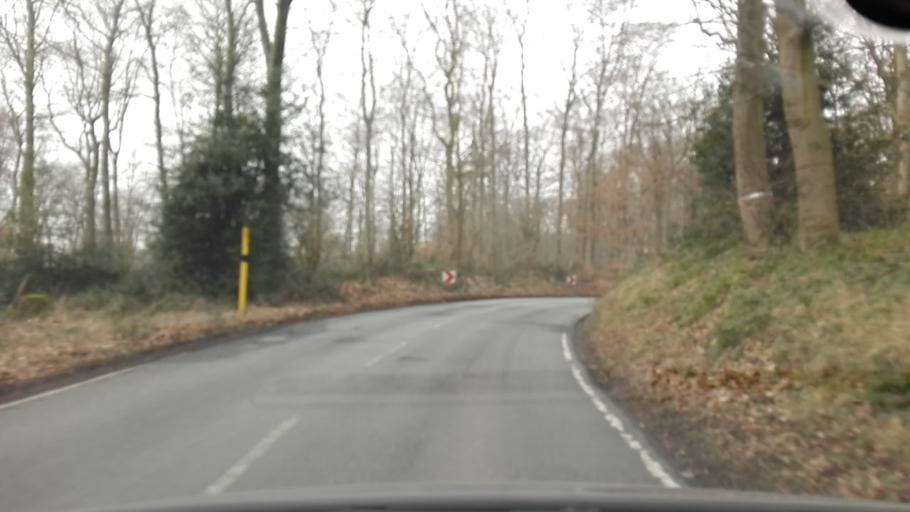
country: DE
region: North Rhine-Westphalia
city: Schwerte
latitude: 51.4606
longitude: 7.5507
